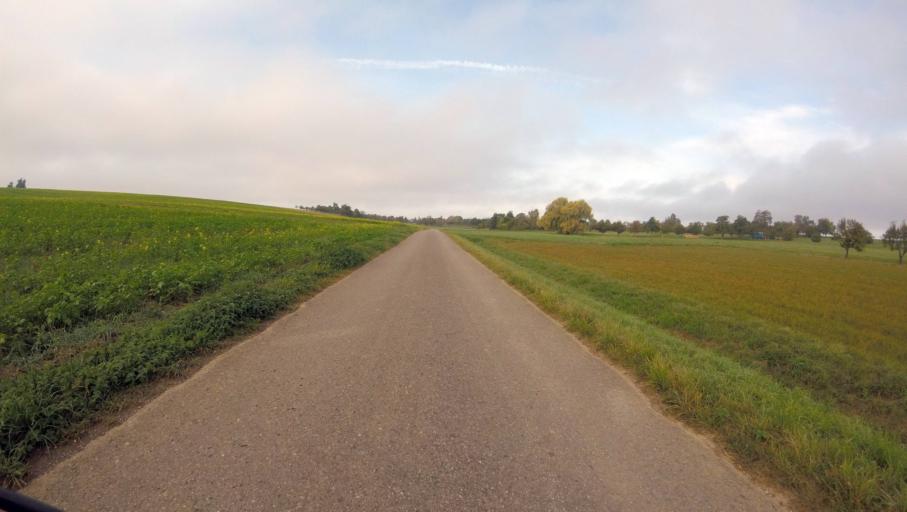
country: DE
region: Baden-Wuerttemberg
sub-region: Regierungsbezirk Stuttgart
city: Motzingen
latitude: 48.5344
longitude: 8.7928
